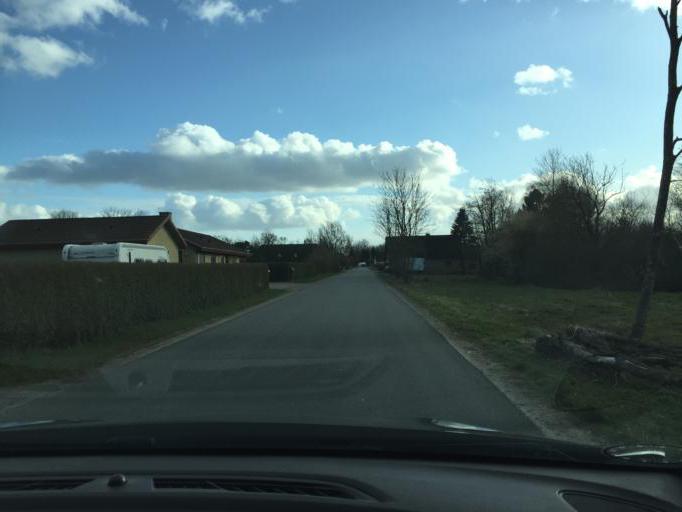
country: DK
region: South Denmark
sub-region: Nyborg Kommune
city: Ullerslev
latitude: 55.3610
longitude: 10.6304
